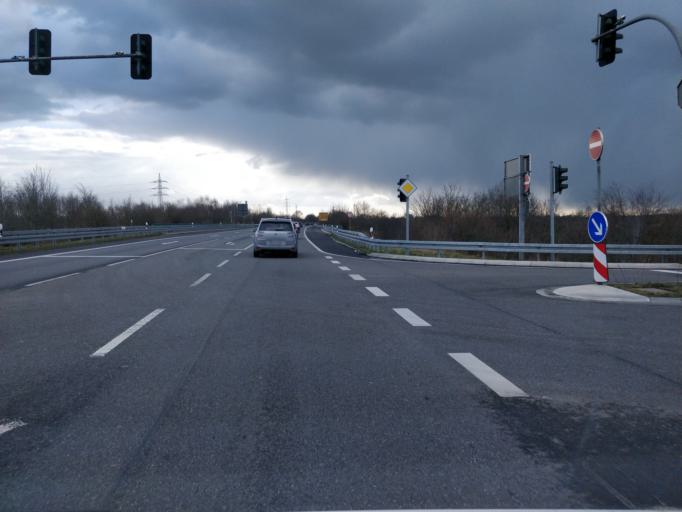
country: DE
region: North Rhine-Westphalia
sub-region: Regierungsbezirk Dusseldorf
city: Bocholt
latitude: 51.8184
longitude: 6.5976
